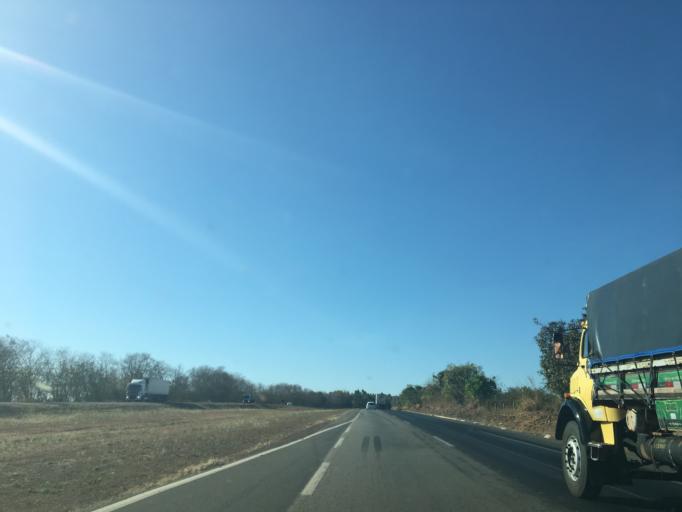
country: BR
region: Goias
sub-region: Hidrolandia
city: Hidrolandia
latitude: -17.0578
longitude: -49.2260
